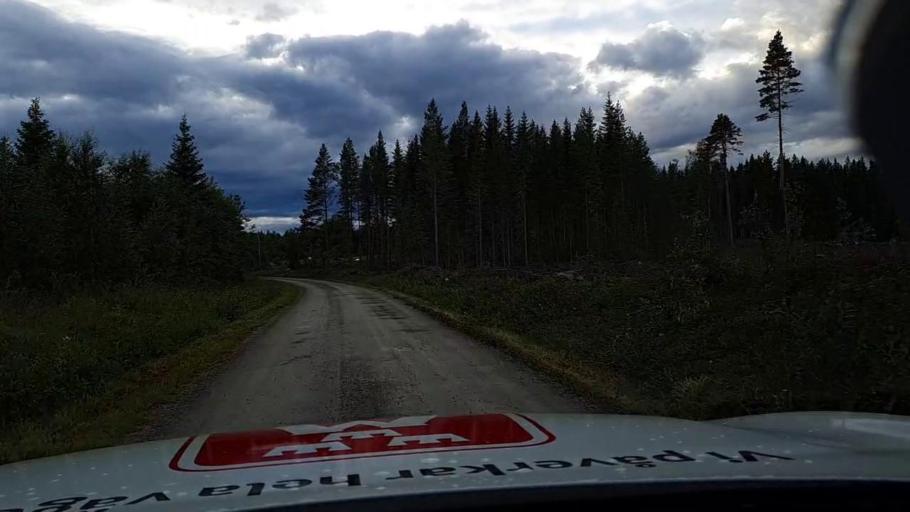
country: SE
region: Jaemtland
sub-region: Bergs Kommun
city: Hoverberg
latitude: 62.8932
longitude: 14.5562
